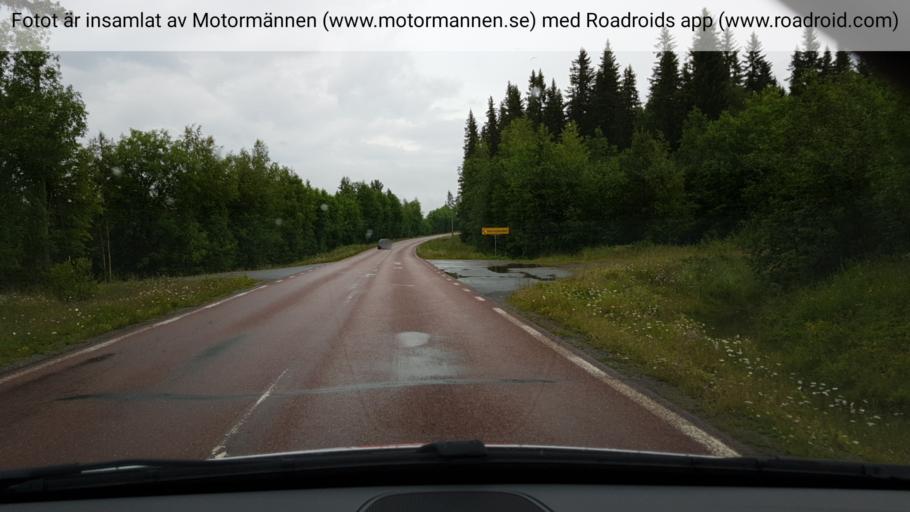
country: SE
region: Vaesterbotten
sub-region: Dorotea Kommun
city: Dorotea
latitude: 64.1031
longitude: 16.0964
